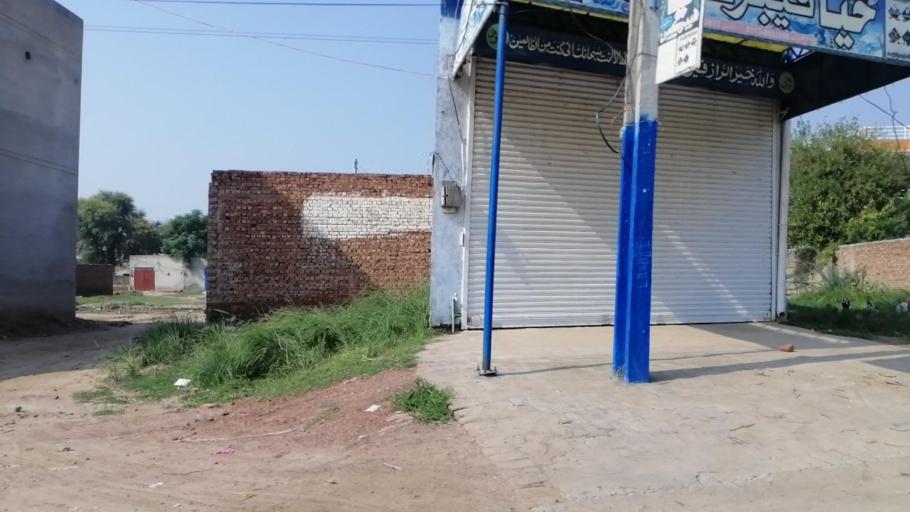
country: PK
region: Punjab
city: Kamalia
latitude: 30.7248
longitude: 72.6631
